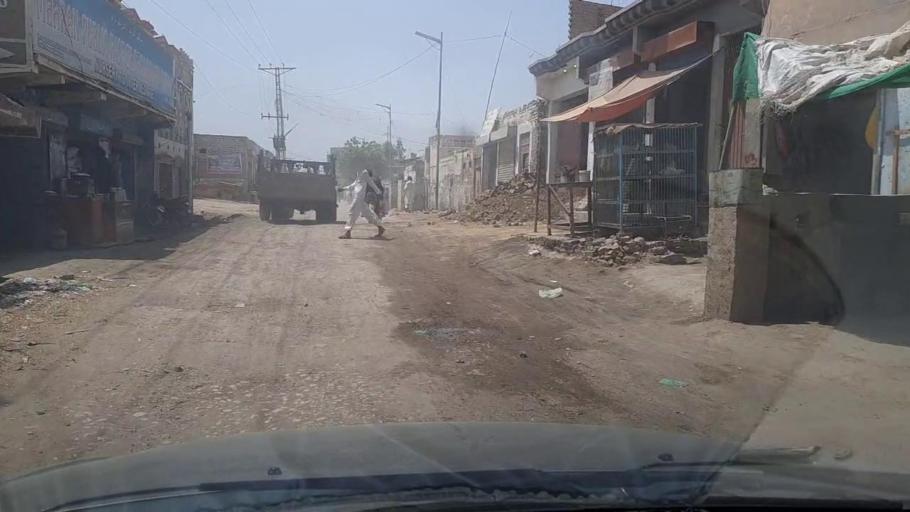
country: PK
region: Sindh
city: Bhiria
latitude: 26.8865
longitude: 68.2793
